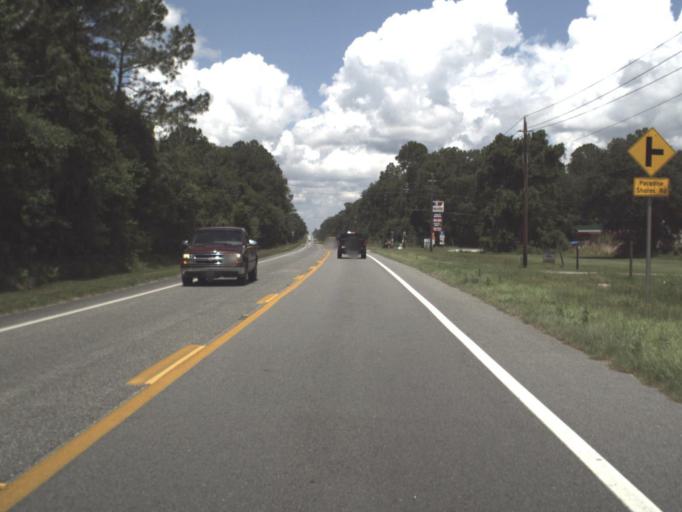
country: US
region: Florida
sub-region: Putnam County
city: Crescent City
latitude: 29.4782
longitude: -81.5434
